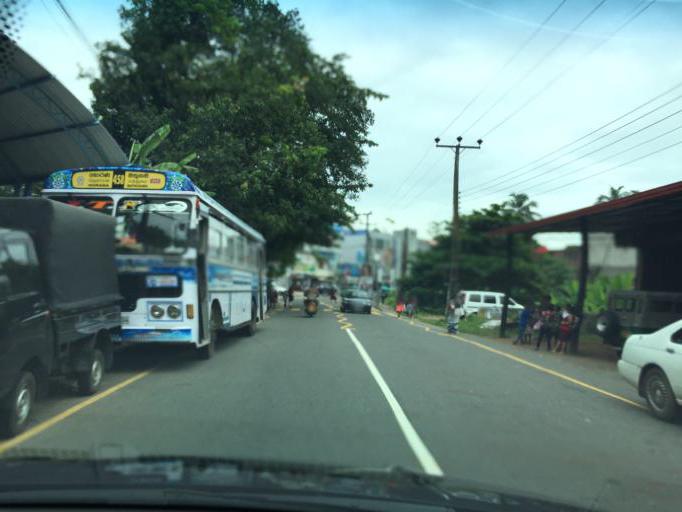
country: LK
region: Western
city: Horana South
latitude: 6.7166
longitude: 80.0656
